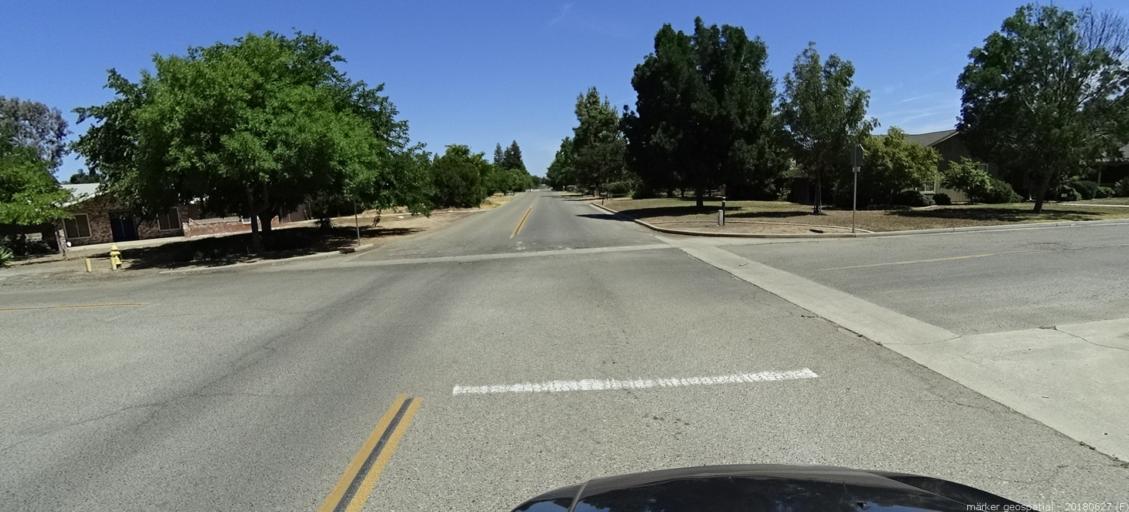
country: US
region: California
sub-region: Madera County
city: Bonadelle Ranchos-Madera Ranchos
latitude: 36.9260
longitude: -119.8882
